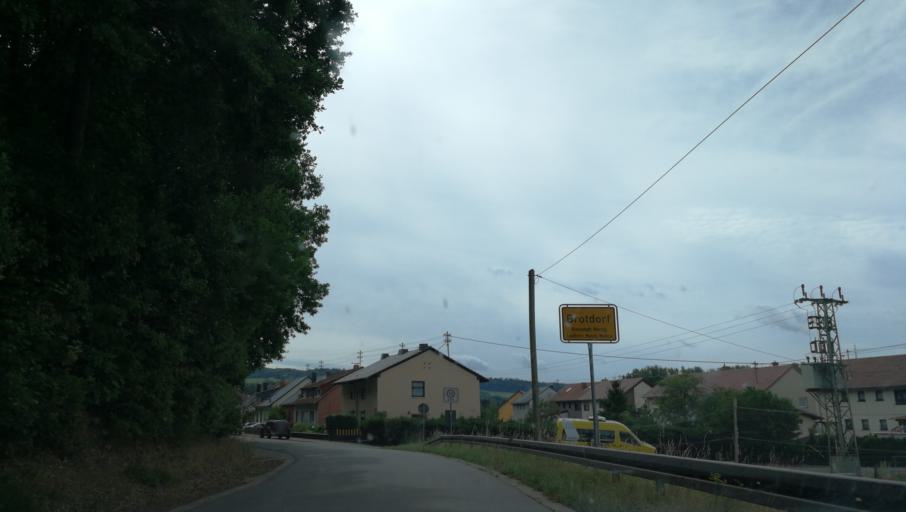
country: DE
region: Saarland
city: Britten
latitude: 49.4788
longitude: 6.6674
